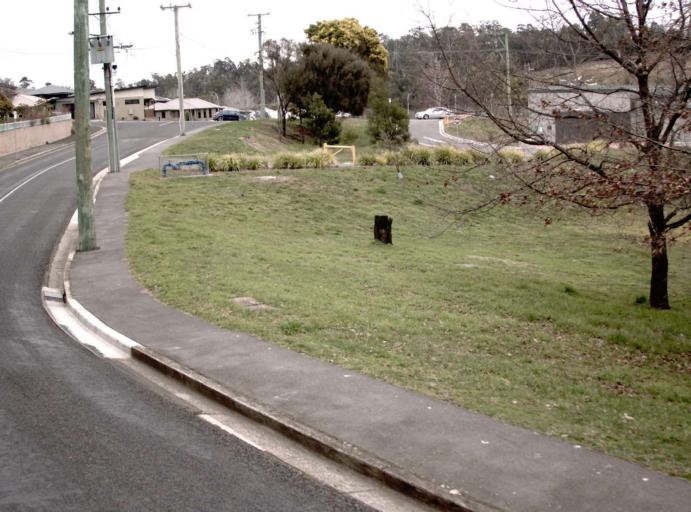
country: AU
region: Tasmania
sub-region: Launceston
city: Newstead
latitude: -41.4516
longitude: 147.1734
